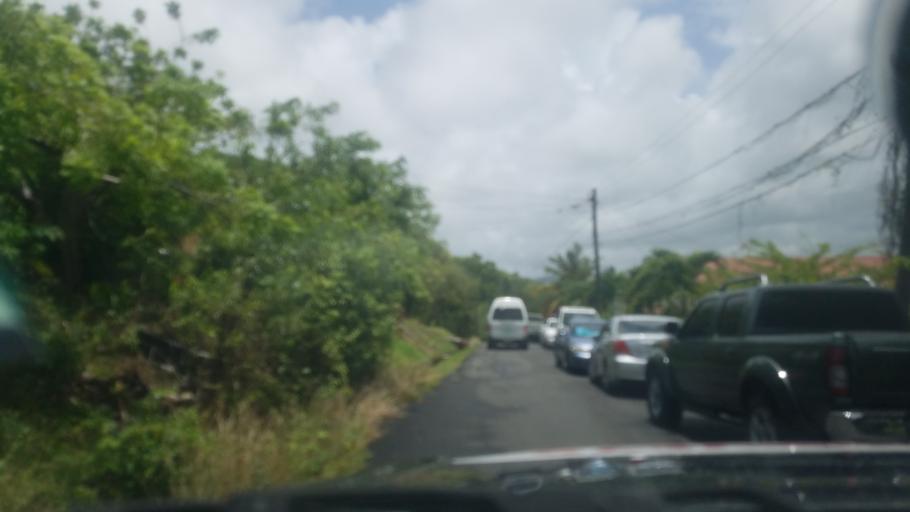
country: LC
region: Laborie Quarter
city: Laborie
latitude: 13.7423
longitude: -60.9609
